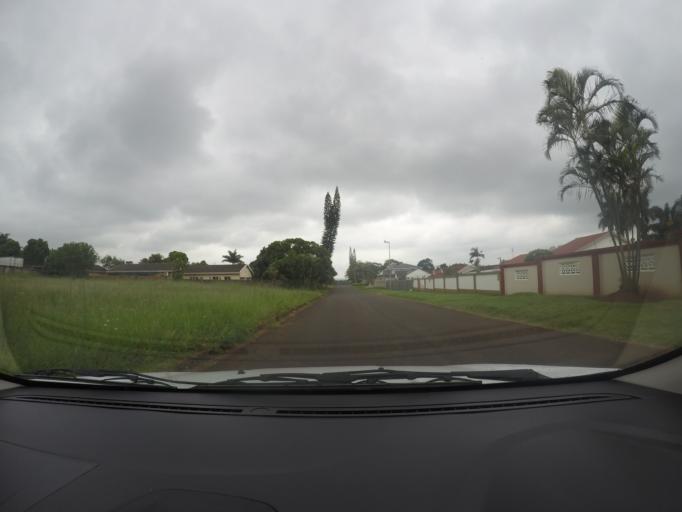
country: ZA
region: KwaZulu-Natal
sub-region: uThungulu District Municipality
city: Empangeni
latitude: -28.7671
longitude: 31.8985
